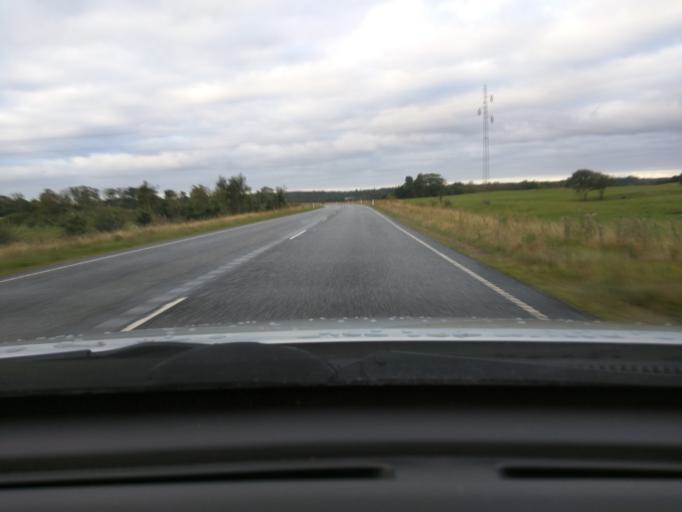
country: DK
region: Central Jutland
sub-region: Silkeborg Kommune
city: Kjellerup
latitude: 56.3340
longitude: 9.3398
